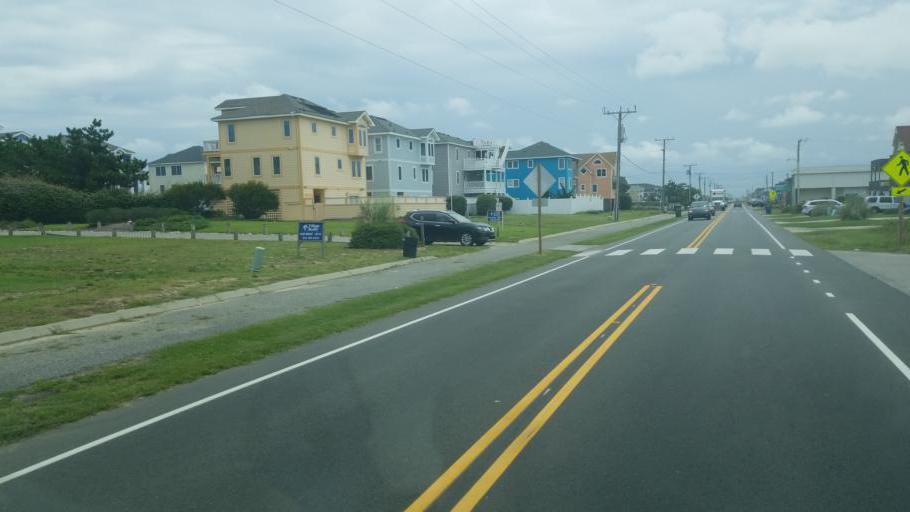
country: US
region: North Carolina
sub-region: Dare County
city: Nags Head
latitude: 35.9904
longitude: -75.6432
